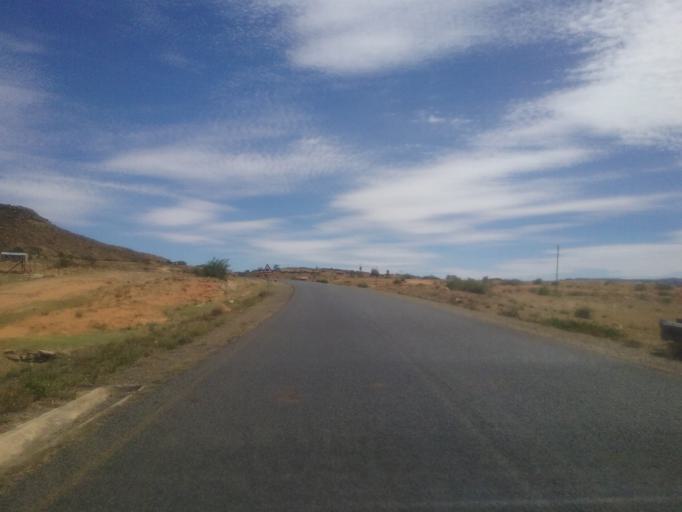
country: LS
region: Mohale's Hoek District
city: Mohale's Hoek
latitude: -30.0729
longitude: 27.4246
